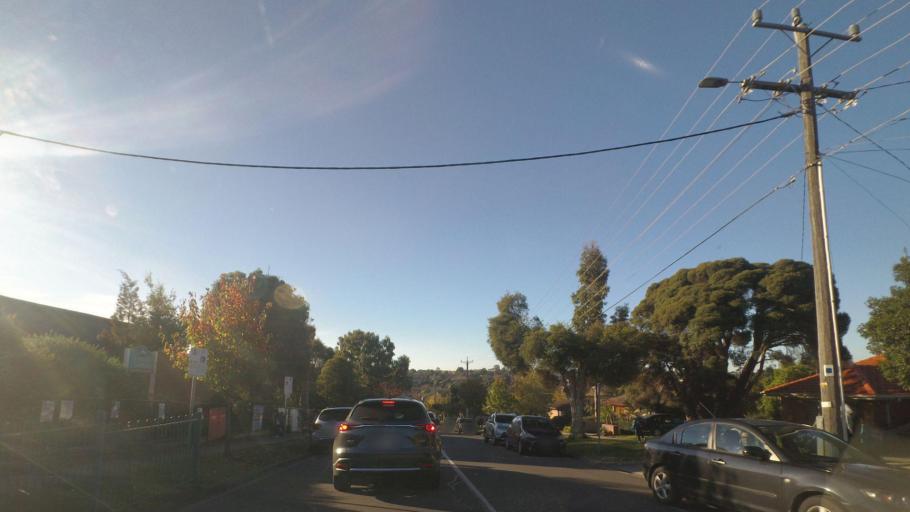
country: AU
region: Victoria
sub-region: Manningham
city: Doncaster East
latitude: -37.7827
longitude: 145.1490
